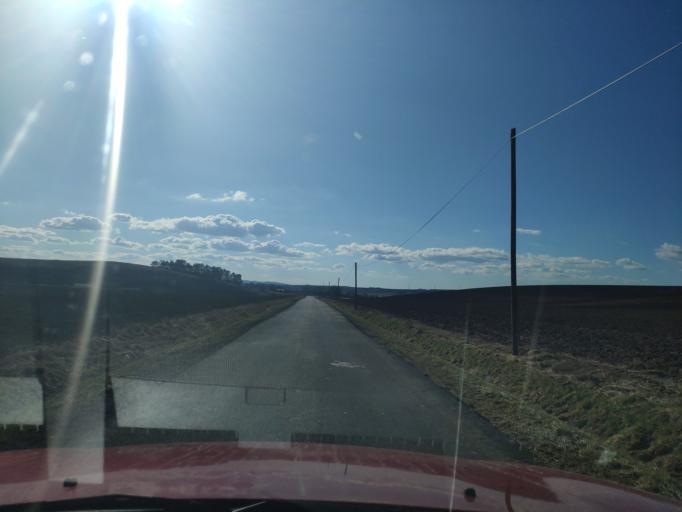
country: HU
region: Borsod-Abauj-Zemplen
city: Putnok
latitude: 48.3663
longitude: 20.3403
